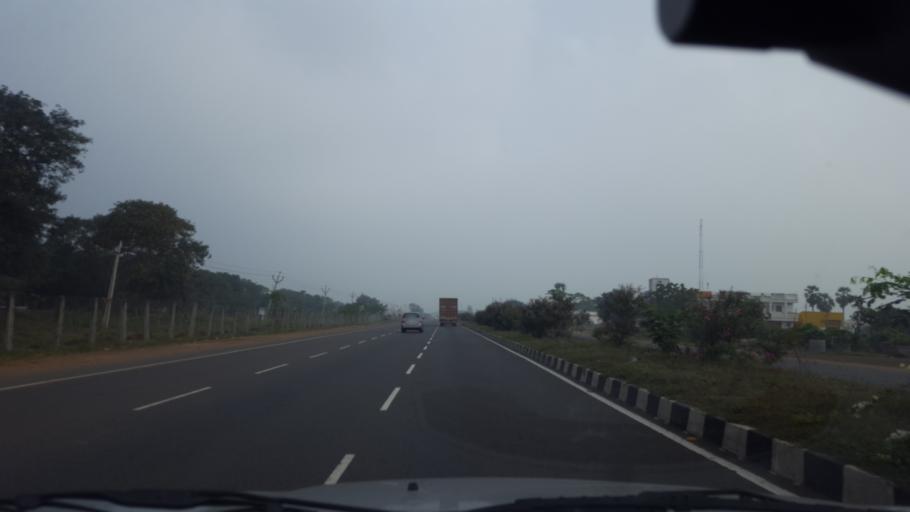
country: IN
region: Andhra Pradesh
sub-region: Prakasam
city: Addanki
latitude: 15.6797
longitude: 80.0175
